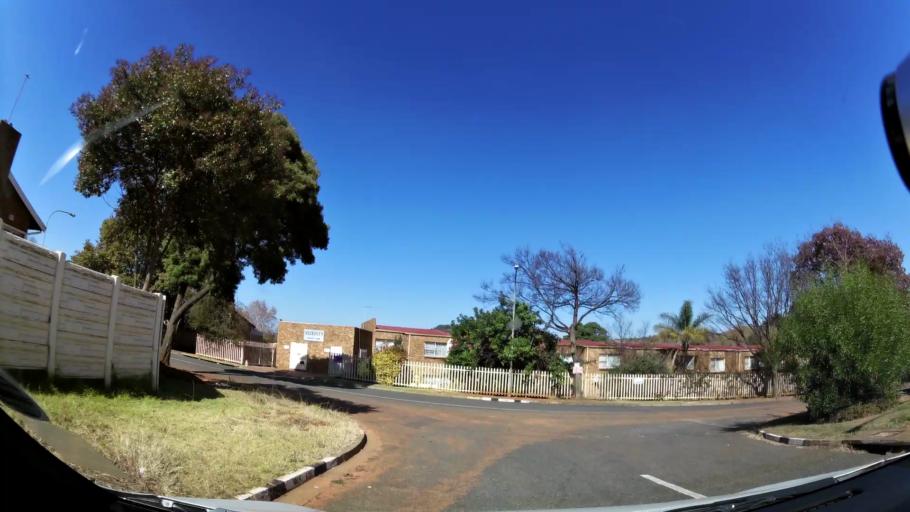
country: ZA
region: Gauteng
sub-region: City of Johannesburg Metropolitan Municipality
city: Johannesburg
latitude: -26.2734
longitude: 27.9863
